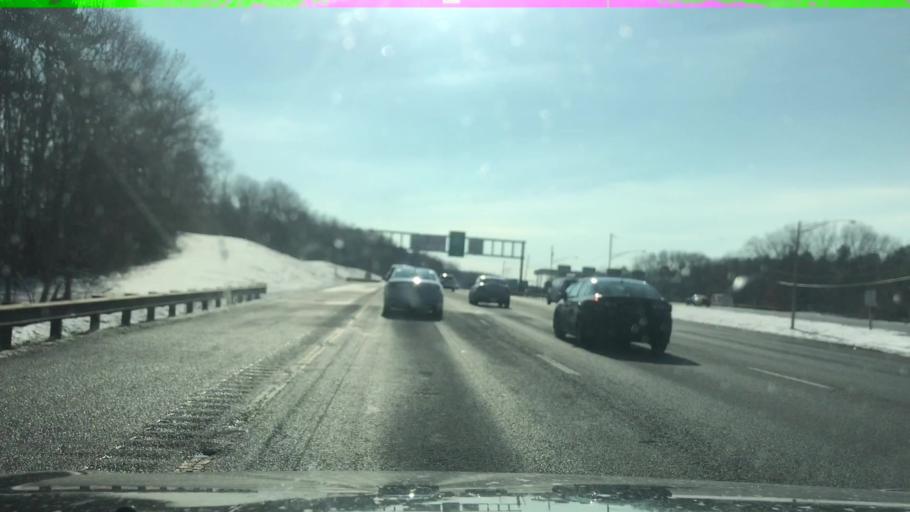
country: US
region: New Jersey
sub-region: Monmouth County
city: Shark River Hills
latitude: 40.1760
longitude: -74.1006
